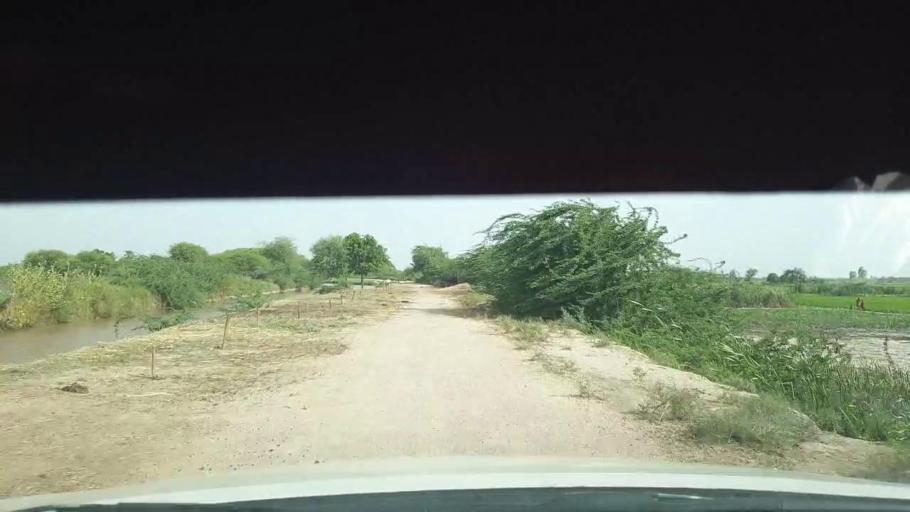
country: PK
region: Sindh
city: Kadhan
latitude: 24.5213
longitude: 69.0036
